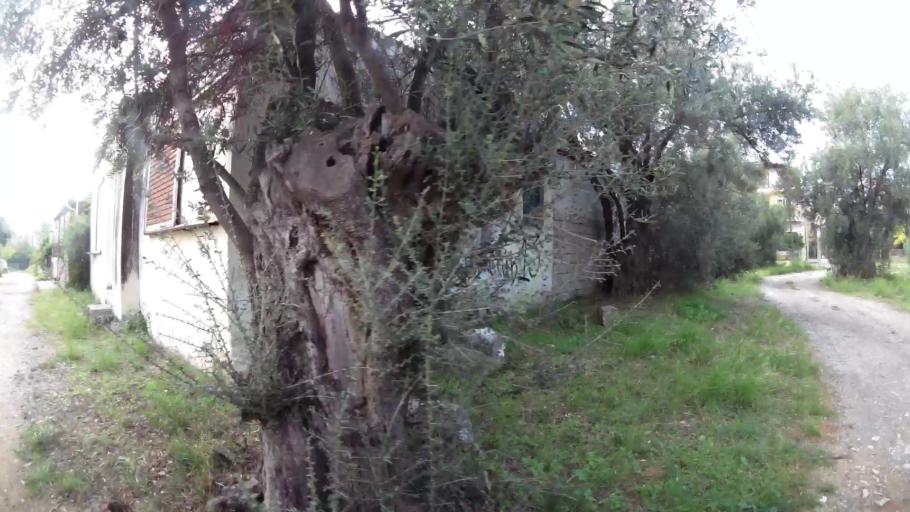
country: GR
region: Attica
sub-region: Nomarchia Dytikis Attikis
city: Zefyri
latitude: 38.0588
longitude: 23.7158
